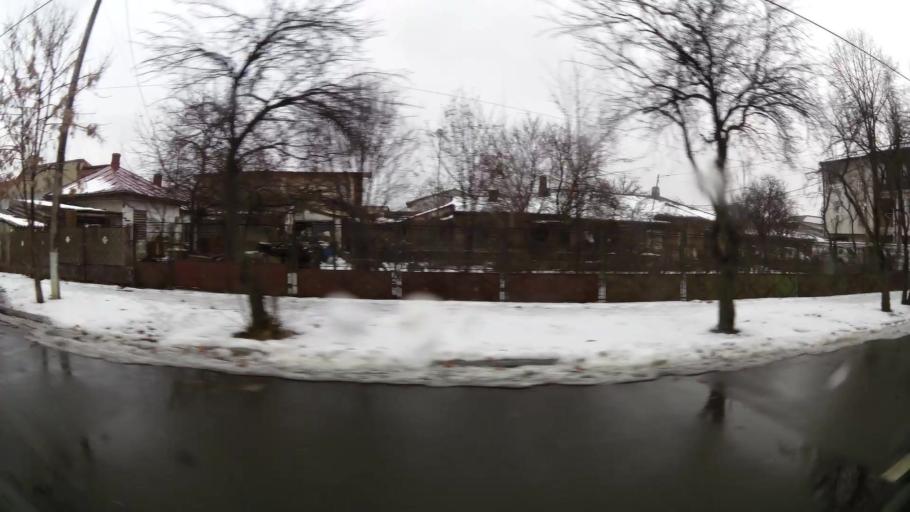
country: RO
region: Ilfov
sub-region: Comuna Chiajna
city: Rosu
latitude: 44.4897
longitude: 26.0212
